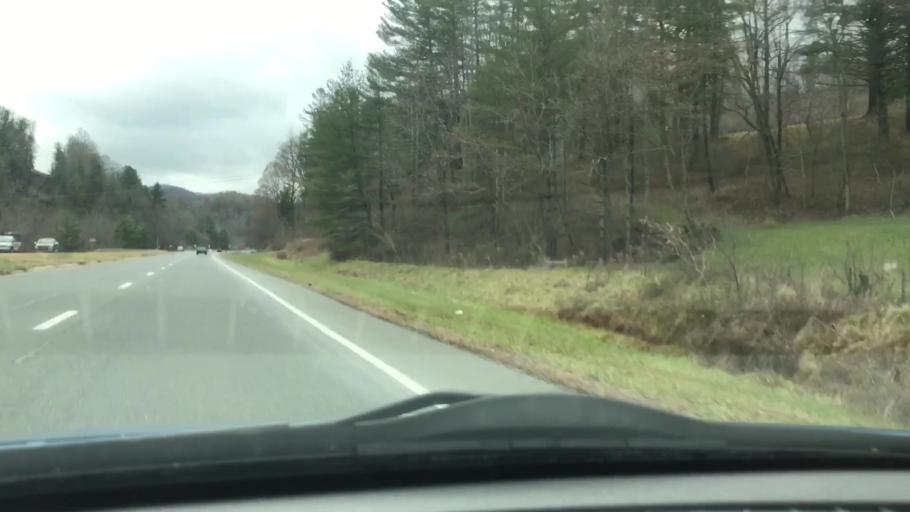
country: US
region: North Carolina
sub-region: Yancey County
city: Burnsville
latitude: 35.9128
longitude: -82.4382
